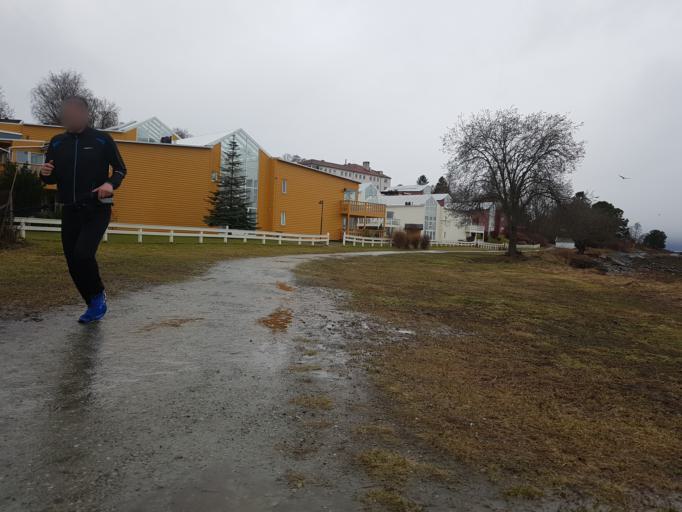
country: NO
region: Sor-Trondelag
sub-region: Trondheim
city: Trondheim
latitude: 63.4360
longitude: 10.4982
